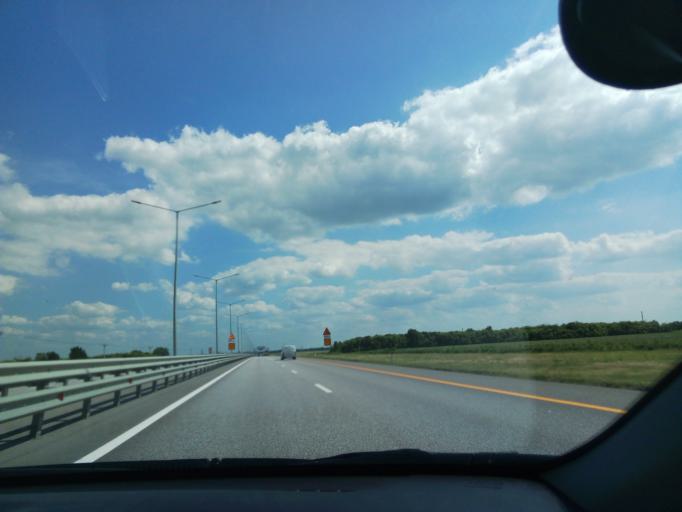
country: RU
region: Voronezj
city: Podkletnoye
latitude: 51.5007
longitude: 39.5217
